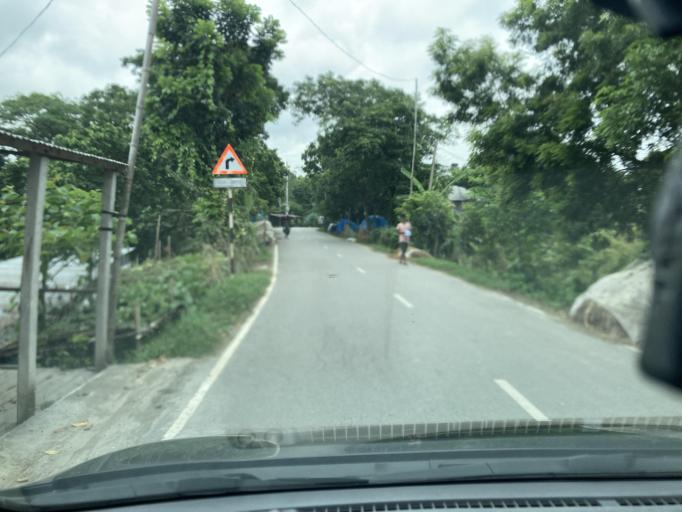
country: BD
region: Dhaka
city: Azimpur
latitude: 23.7806
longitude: 90.2091
